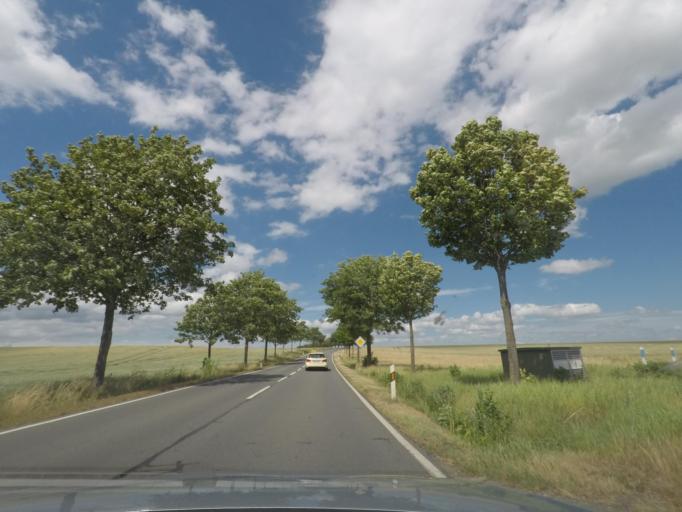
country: DE
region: Saxony-Anhalt
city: Gross Quenstedt
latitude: 51.9370
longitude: 11.1200
